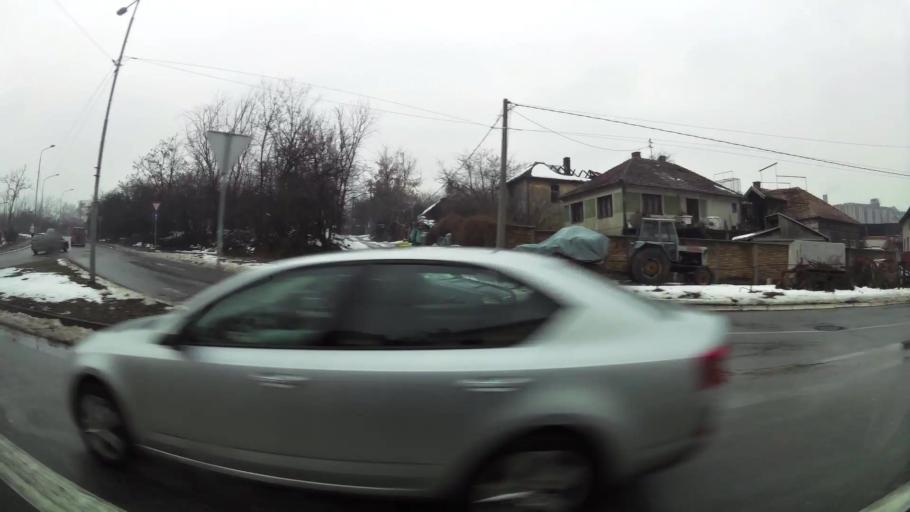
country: RS
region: Central Serbia
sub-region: Belgrade
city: Vozdovac
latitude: 44.7655
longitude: 20.4918
